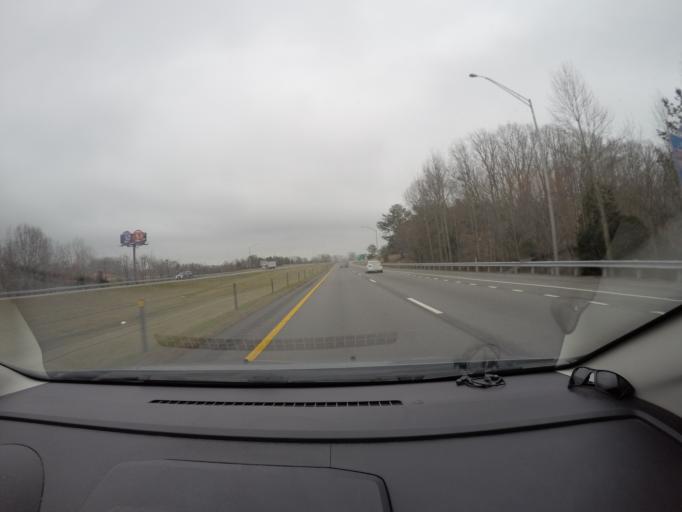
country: US
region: Tennessee
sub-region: Coffee County
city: Manchester
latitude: 35.4973
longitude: -86.0821
